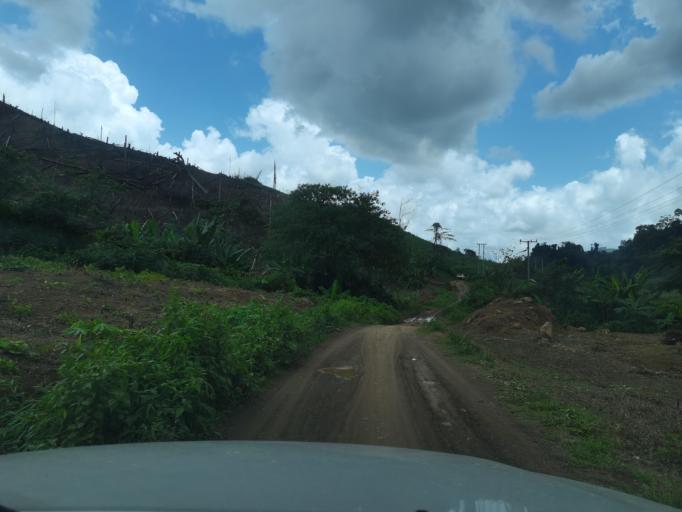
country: LA
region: Loungnamtha
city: Muang Long
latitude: 20.7650
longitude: 101.0177
